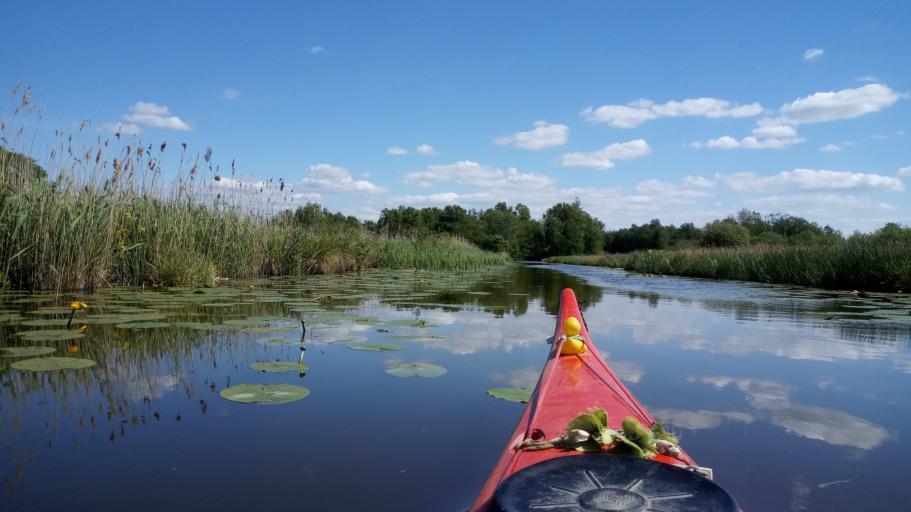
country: NL
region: South Holland
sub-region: Gemeente Nieuwkoop
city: Nieuwkoop
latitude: 52.1381
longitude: 4.7832
